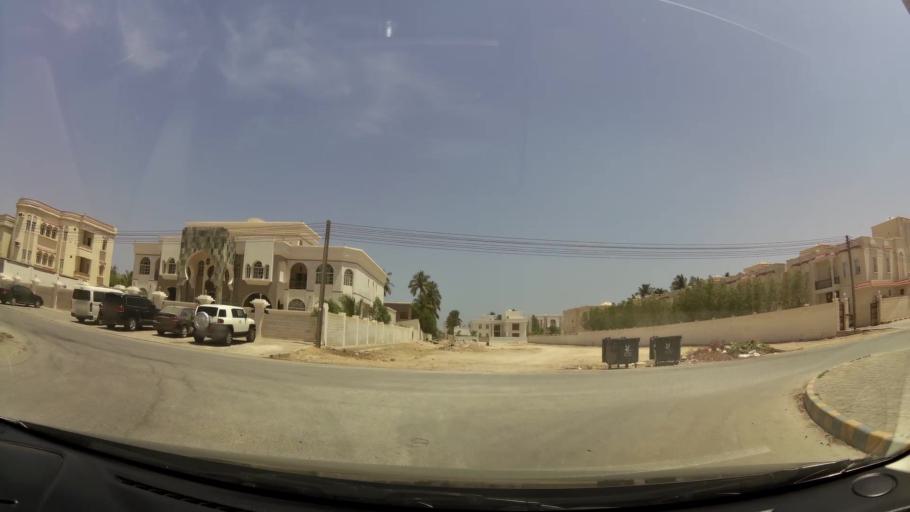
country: OM
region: Zufar
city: Salalah
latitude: 17.0584
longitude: 54.1533
